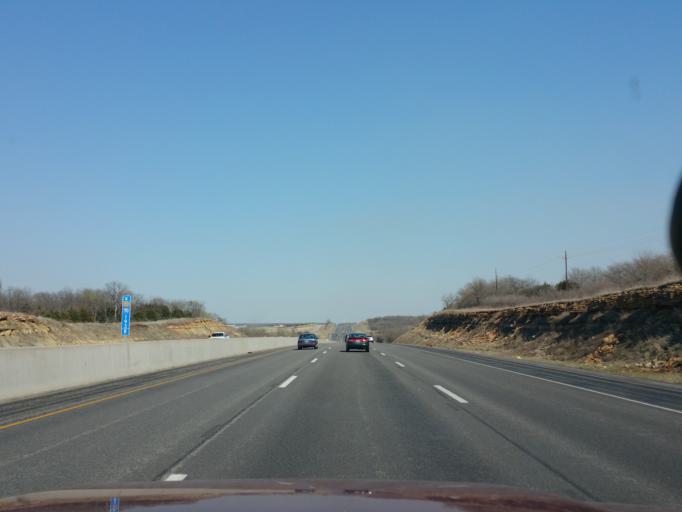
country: US
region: Kansas
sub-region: Douglas County
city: Lawrence
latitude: 39.0000
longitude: -95.4070
